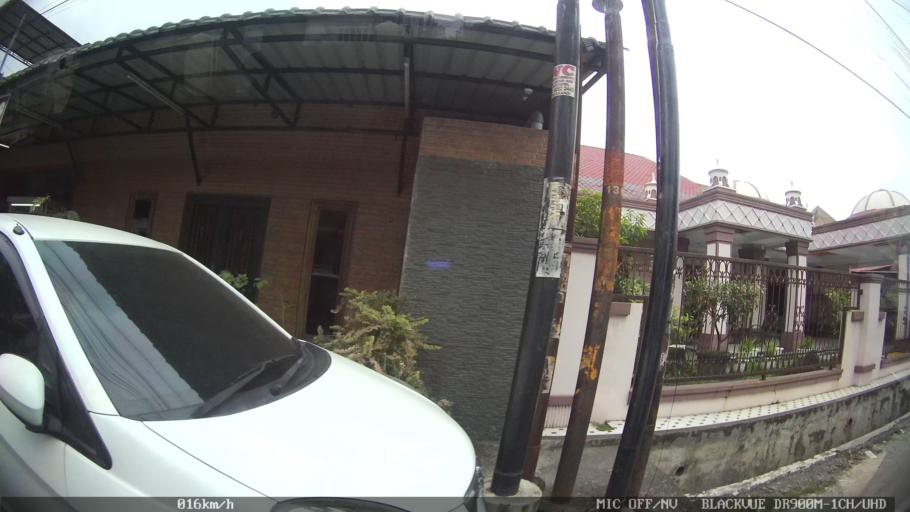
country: ID
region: North Sumatra
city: Medan
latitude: 3.5751
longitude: 98.7018
